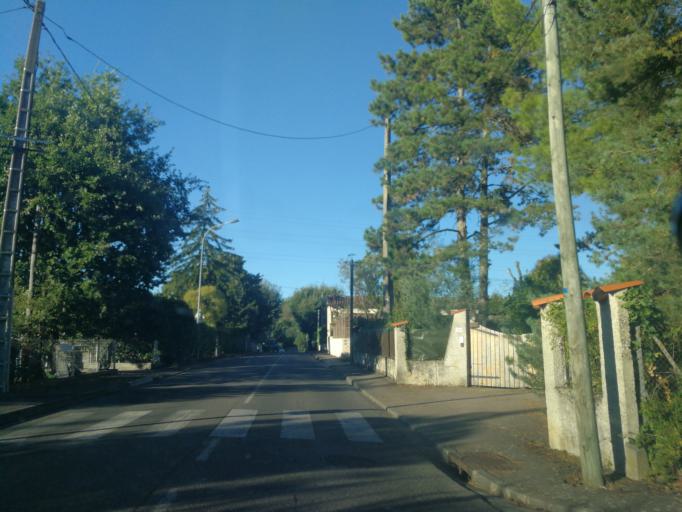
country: FR
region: Midi-Pyrenees
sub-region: Departement de la Haute-Garonne
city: Balma
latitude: 43.6146
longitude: 1.5031
